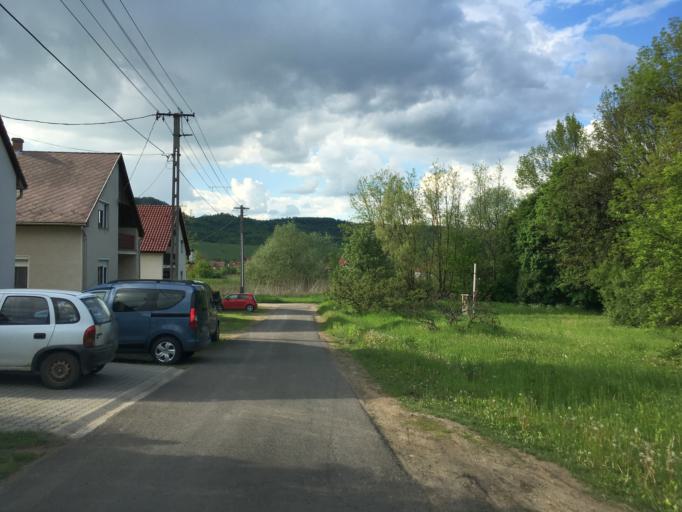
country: HU
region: Nograd
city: Matraverebely
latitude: 47.9696
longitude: 19.7743
